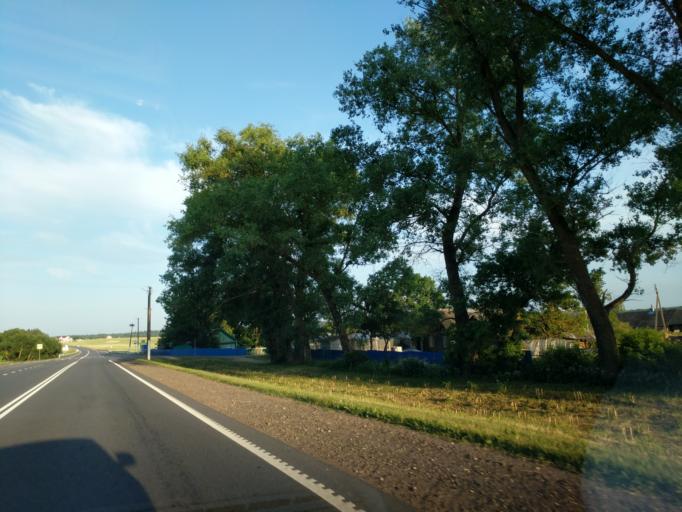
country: BY
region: Minsk
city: Syomkava
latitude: 54.1021
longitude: 27.4787
